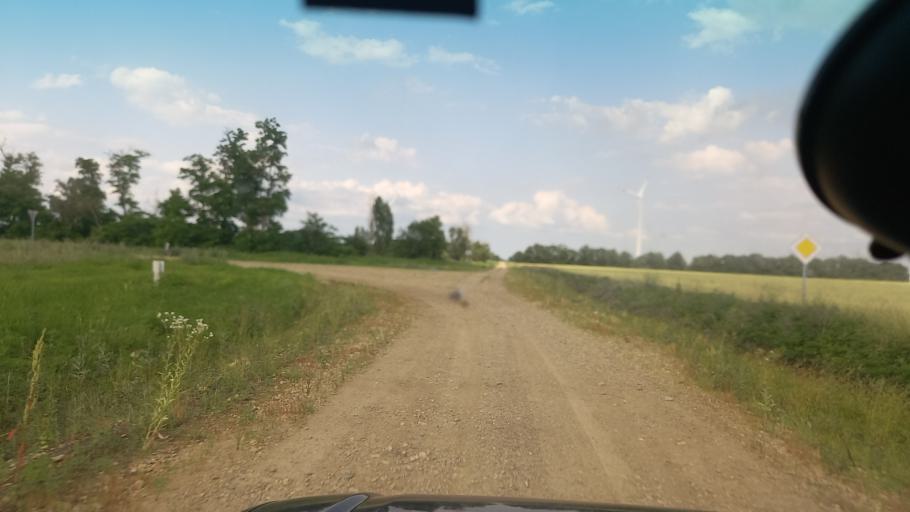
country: RU
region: Adygeya
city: Giaginskaya
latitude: 44.9480
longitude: 40.1245
